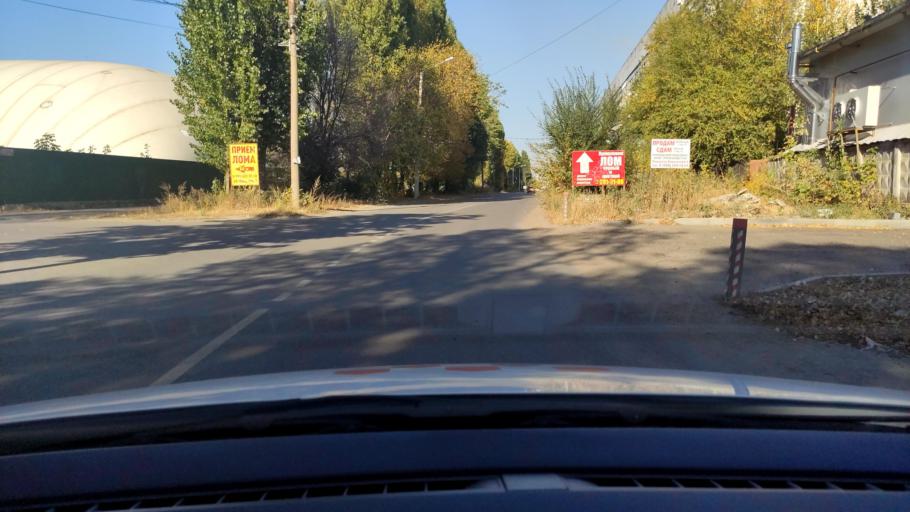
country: RU
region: Voronezj
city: Voronezh
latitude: 51.6774
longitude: 39.1443
